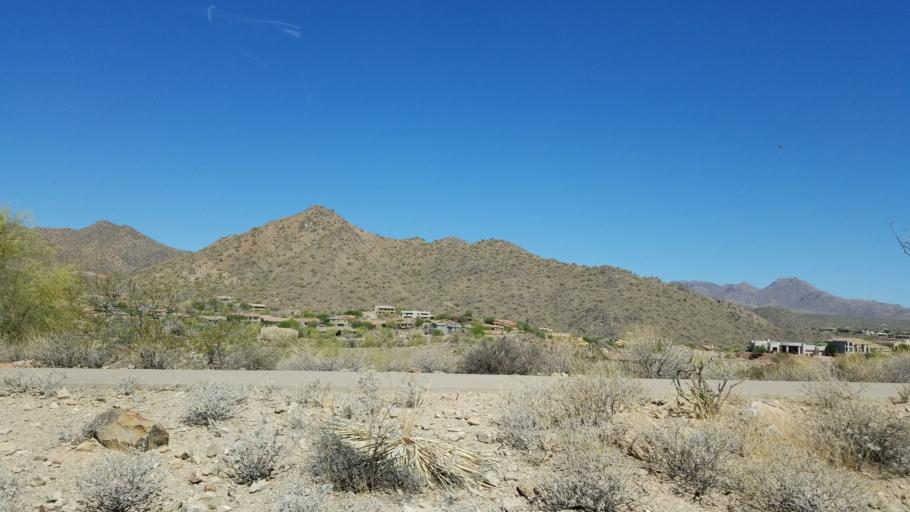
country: US
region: Arizona
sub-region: Maricopa County
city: Fountain Hills
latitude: 33.6062
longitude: -111.7482
